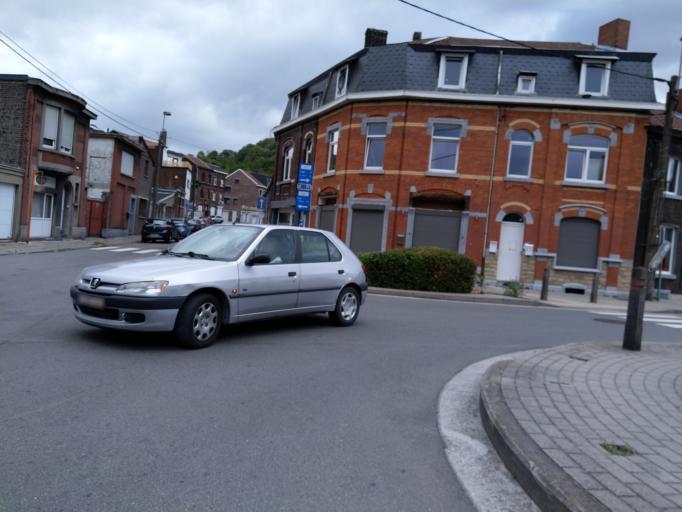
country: BE
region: Wallonia
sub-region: Province de Liege
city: Saint-Nicolas
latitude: 50.6200
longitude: 5.5288
